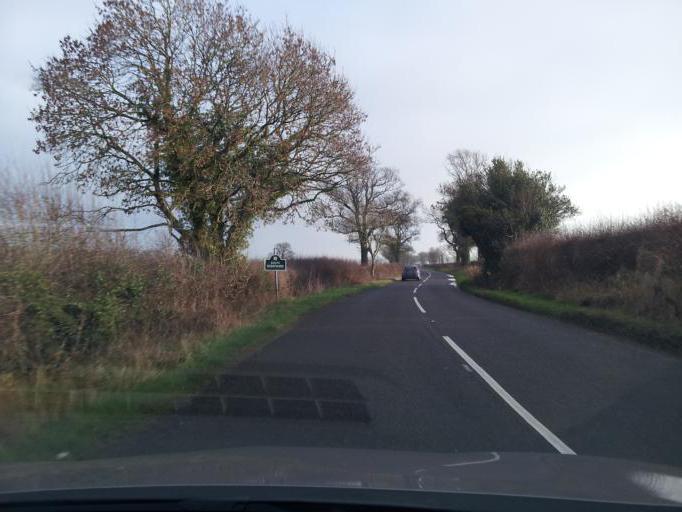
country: GB
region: England
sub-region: Derbyshire
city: Rodsley
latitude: 52.8774
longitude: -1.7391
